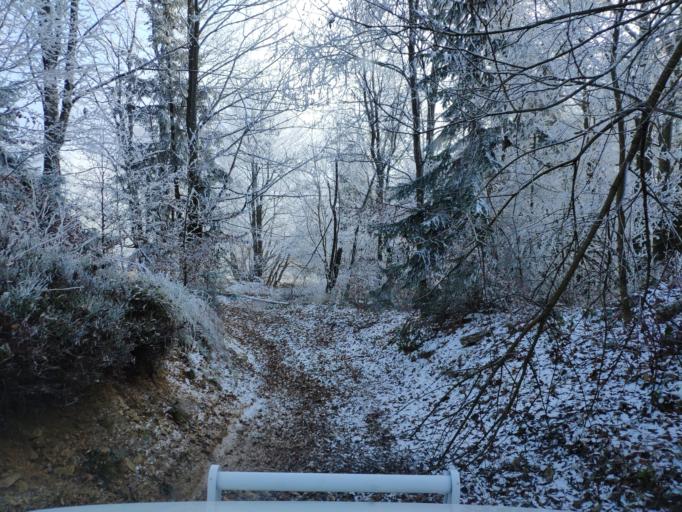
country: SK
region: Kosicky
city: Dobsina
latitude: 48.8131
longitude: 20.4792
